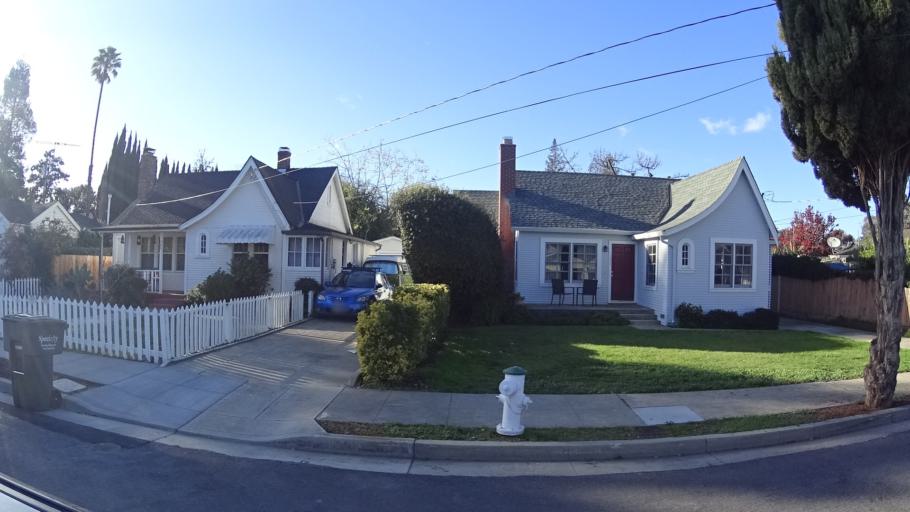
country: US
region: California
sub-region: Santa Clara County
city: Sunnyvale
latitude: 37.3747
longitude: -122.0384
